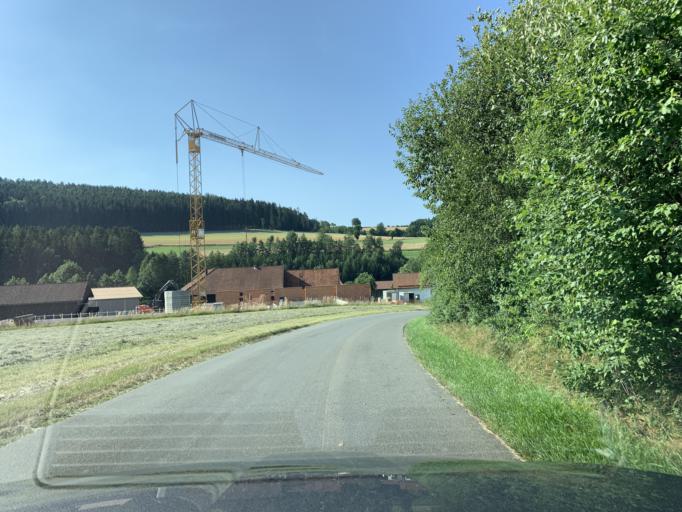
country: DE
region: Bavaria
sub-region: Upper Palatinate
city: Dieterskirchen
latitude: 49.4177
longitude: 12.4299
